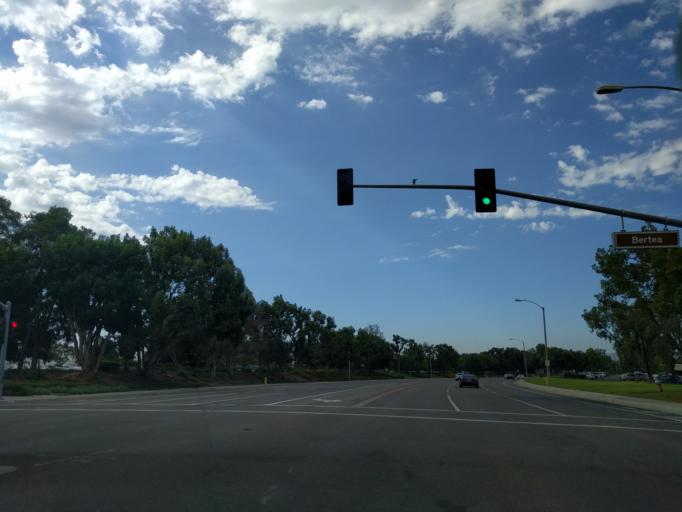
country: US
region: California
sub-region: Orange County
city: Lake Forest
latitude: 33.6575
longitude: -117.7106
